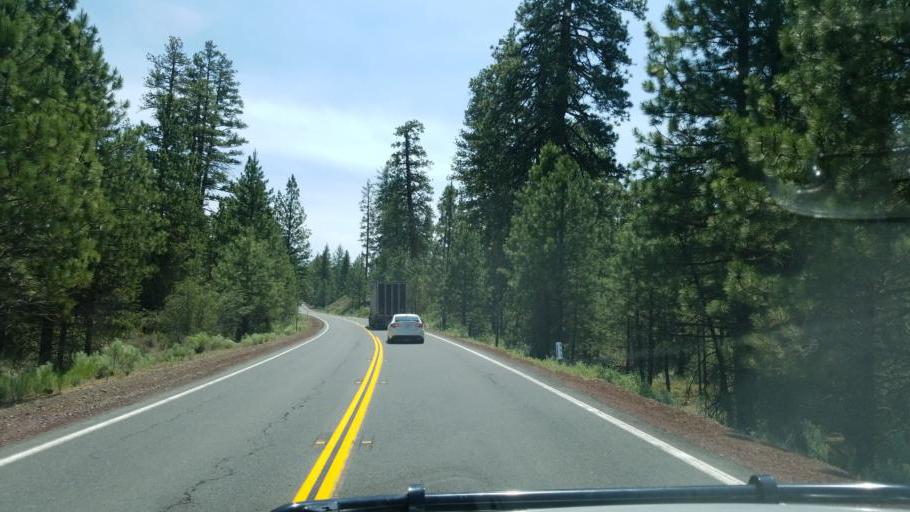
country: US
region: California
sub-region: Shasta County
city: Burney
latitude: 40.6890
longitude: -121.3810
